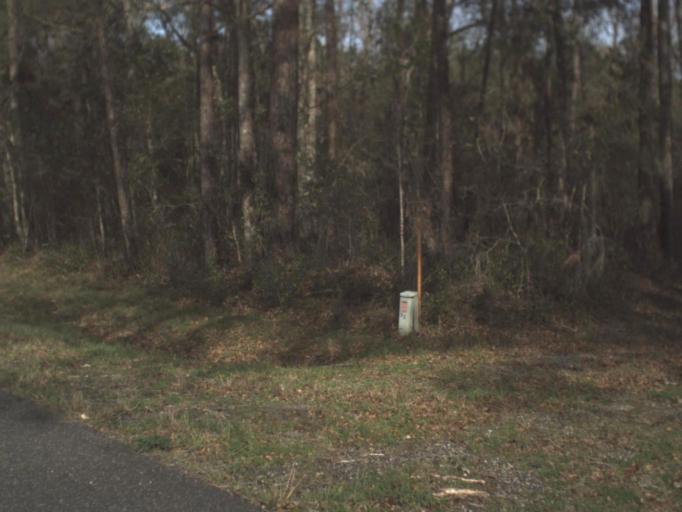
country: US
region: Florida
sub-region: Jefferson County
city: Monticello
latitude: 30.4419
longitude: -83.9028
